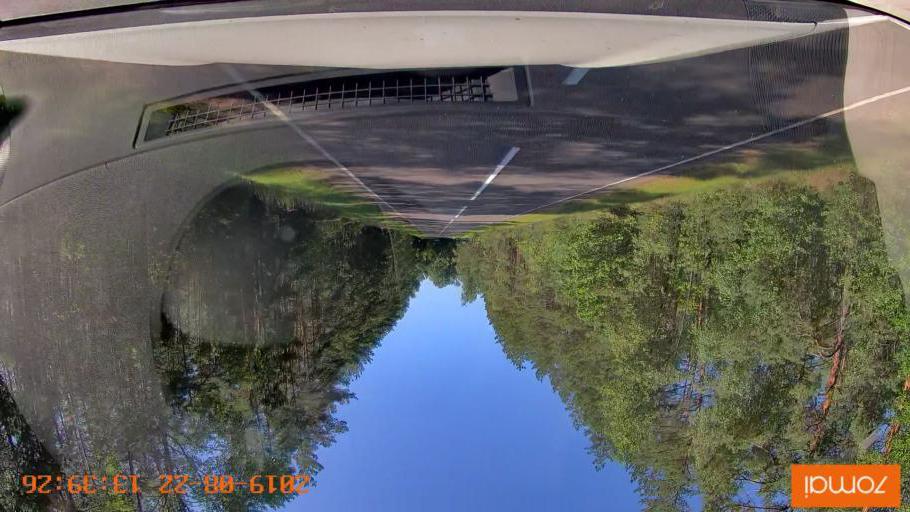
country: BY
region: Minsk
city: Staryya Darohi
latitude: 53.2275
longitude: 28.3494
